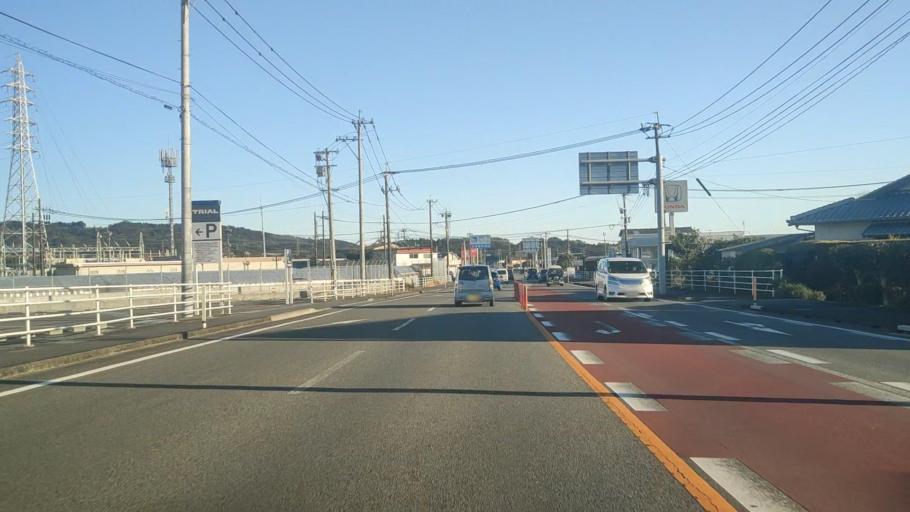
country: JP
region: Miyazaki
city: Takanabe
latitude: 32.2550
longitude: 131.5542
